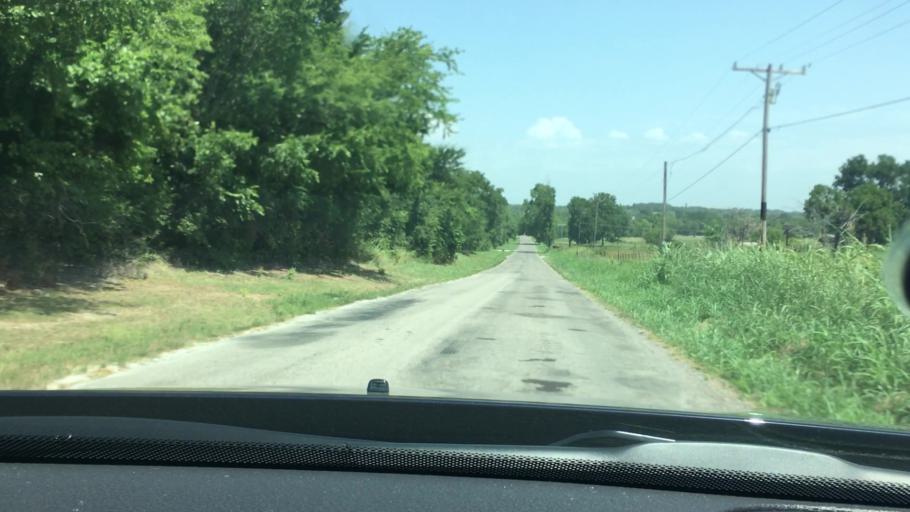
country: US
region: Oklahoma
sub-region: Pontotoc County
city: Byng
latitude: 34.8310
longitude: -96.6698
